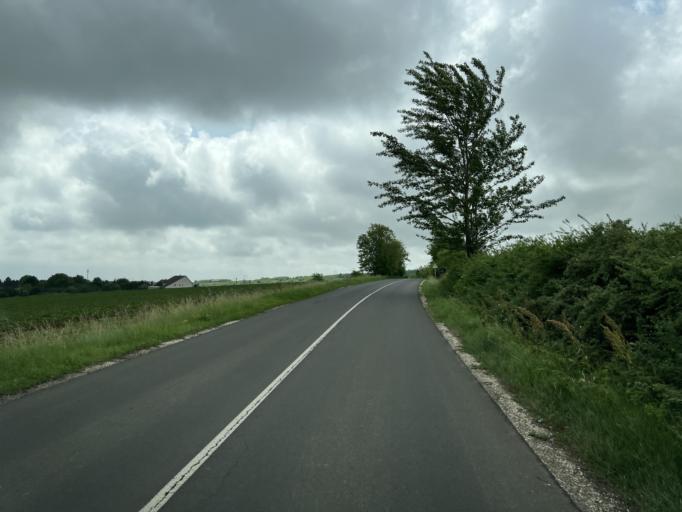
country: HU
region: Pest
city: Kartal
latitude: 47.7272
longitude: 19.5333
